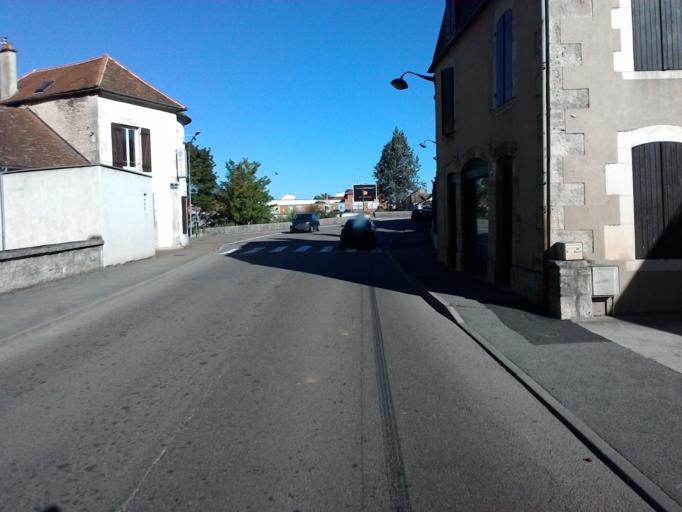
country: FR
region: Bourgogne
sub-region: Departement de la Cote-d'Or
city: Chatillon-sur-Seine
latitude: 47.8647
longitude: 4.5744
